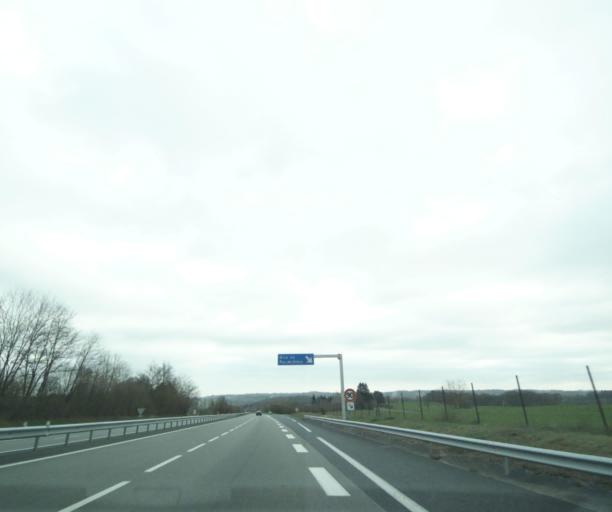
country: FR
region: Limousin
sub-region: Departement de la Correze
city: Vigeois
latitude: 45.3644
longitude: 1.5707
